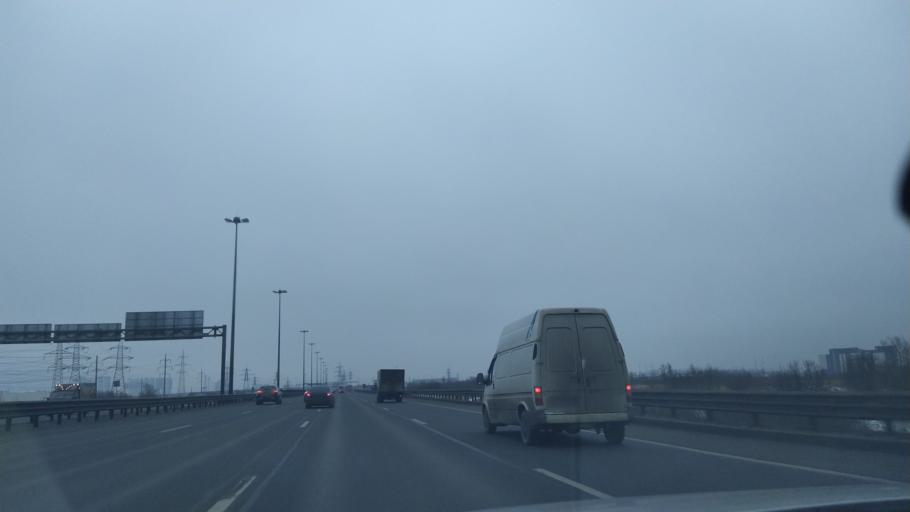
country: RU
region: Leningrad
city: Murino
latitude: 60.0264
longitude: 30.4489
